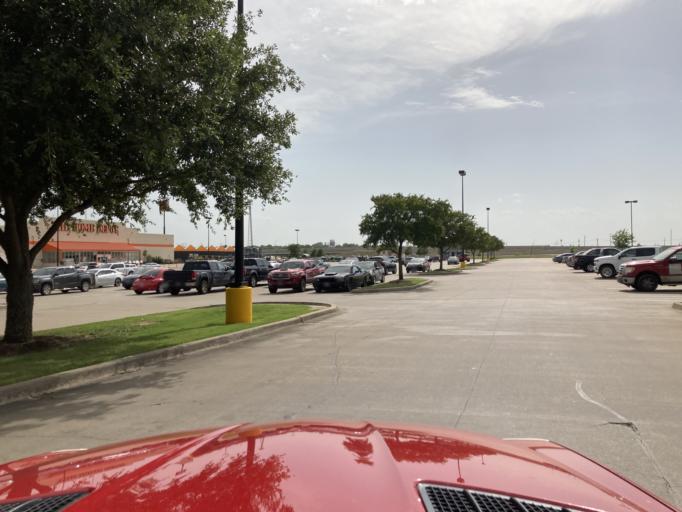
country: US
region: Texas
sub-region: Navarro County
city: Corsicana
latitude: 32.0666
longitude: -96.4486
